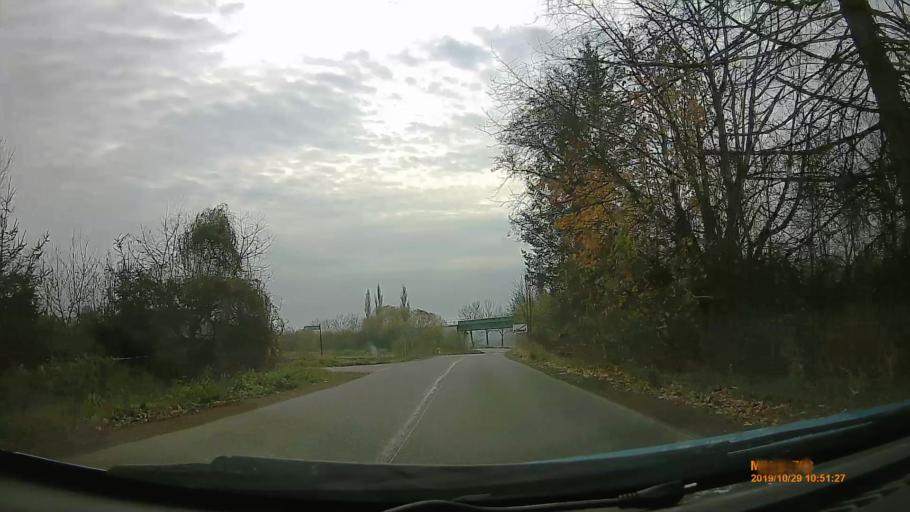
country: PL
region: Lower Silesian Voivodeship
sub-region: Powiat klodzki
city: Nowa Ruda
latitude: 50.5441
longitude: 16.4628
